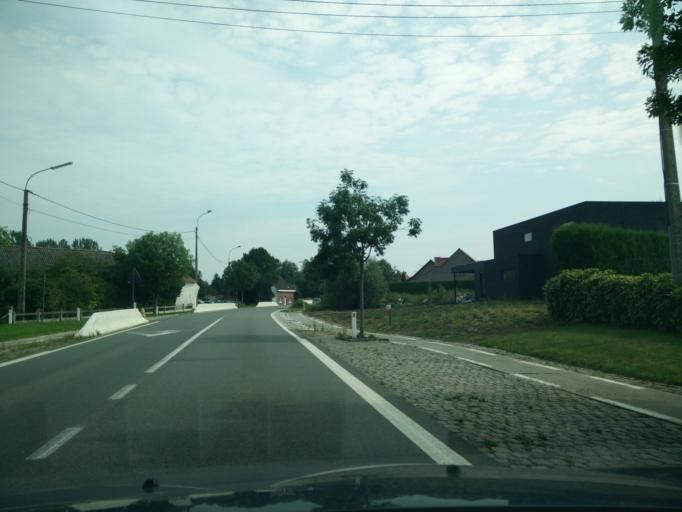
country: BE
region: Flanders
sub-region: Provincie Oost-Vlaanderen
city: Gavere
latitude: 50.9001
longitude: 3.7223
